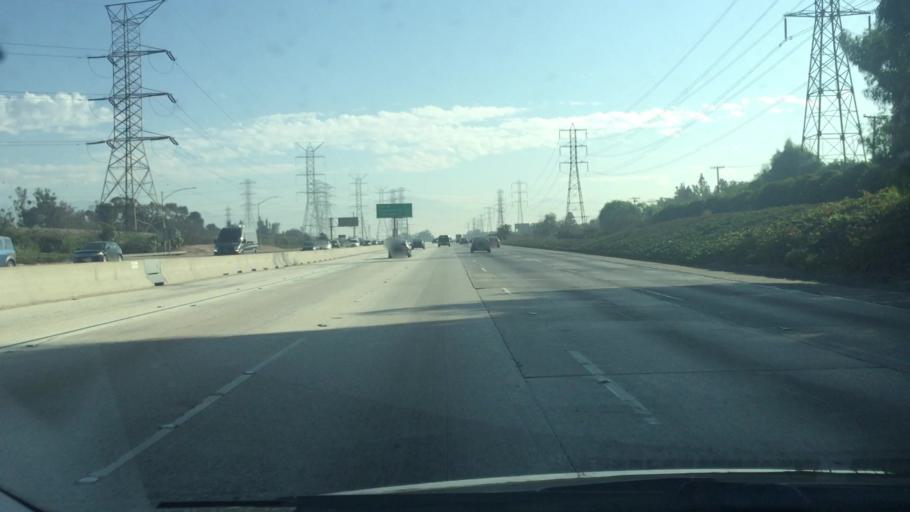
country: US
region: California
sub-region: Los Angeles County
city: South El Monte
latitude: 34.0181
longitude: -118.0524
